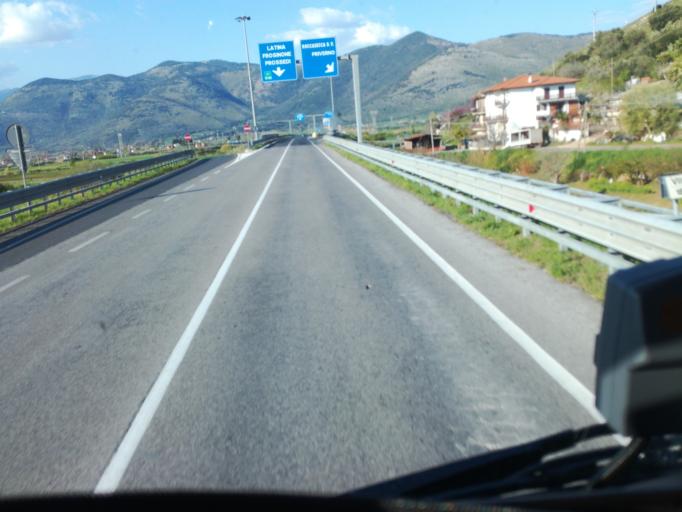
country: IT
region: Latium
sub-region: Provincia di Latina
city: Roccasecca dei Volsci
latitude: 41.4818
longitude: 13.2037
